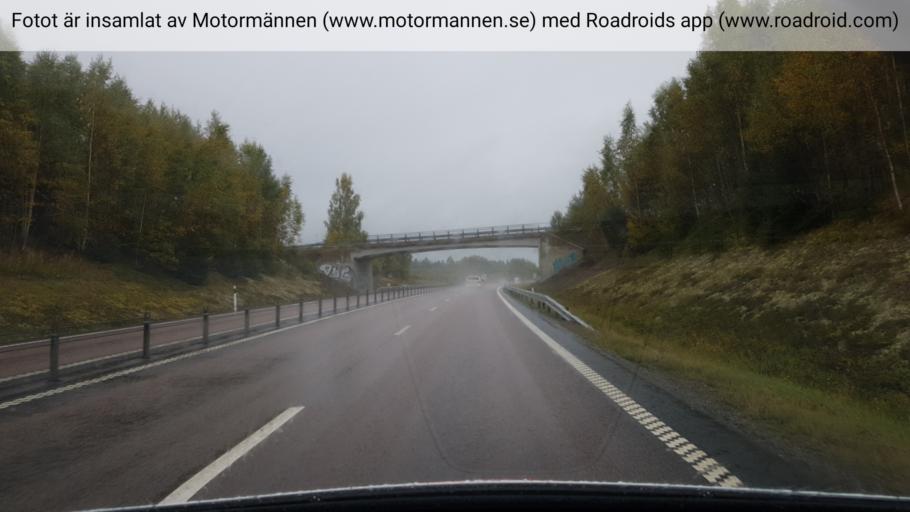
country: SE
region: Gaevleborg
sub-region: Hudiksvalls Kommun
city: Hudiksvall
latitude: 61.7612
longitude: 17.0923
